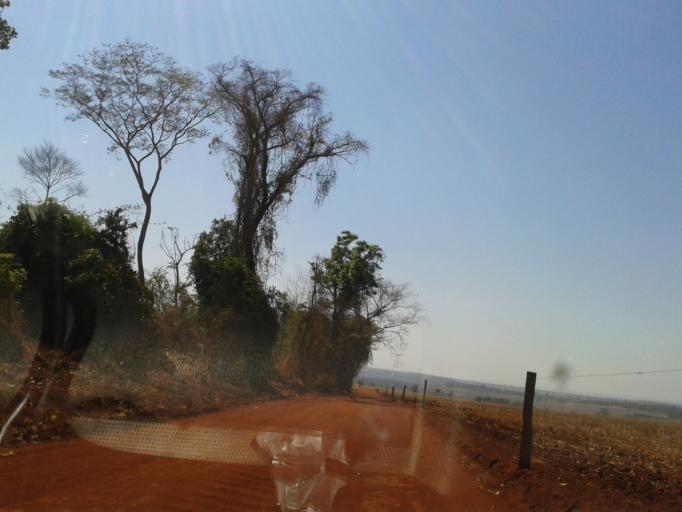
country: BR
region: Minas Gerais
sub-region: Capinopolis
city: Capinopolis
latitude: -18.6180
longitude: -49.4729
